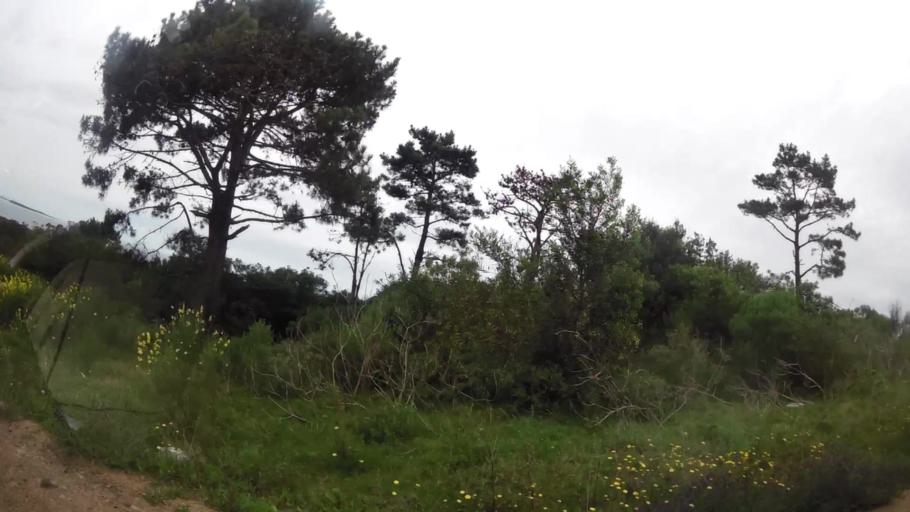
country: UY
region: Maldonado
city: Maldonado
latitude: -34.9024
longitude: -55.0401
